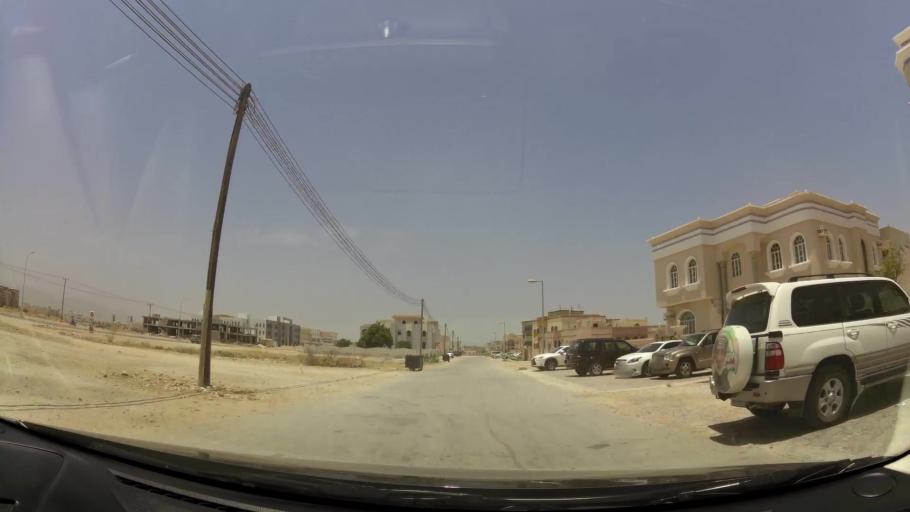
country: OM
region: Zufar
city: Salalah
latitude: 17.0849
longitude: 54.1536
